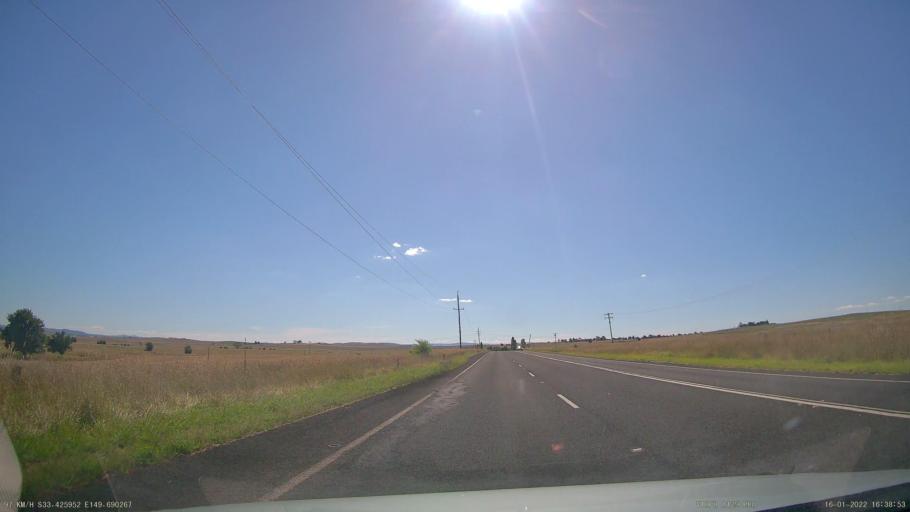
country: AU
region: New South Wales
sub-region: Bathurst Regional
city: Kelso
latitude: -33.4262
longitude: 149.6896
